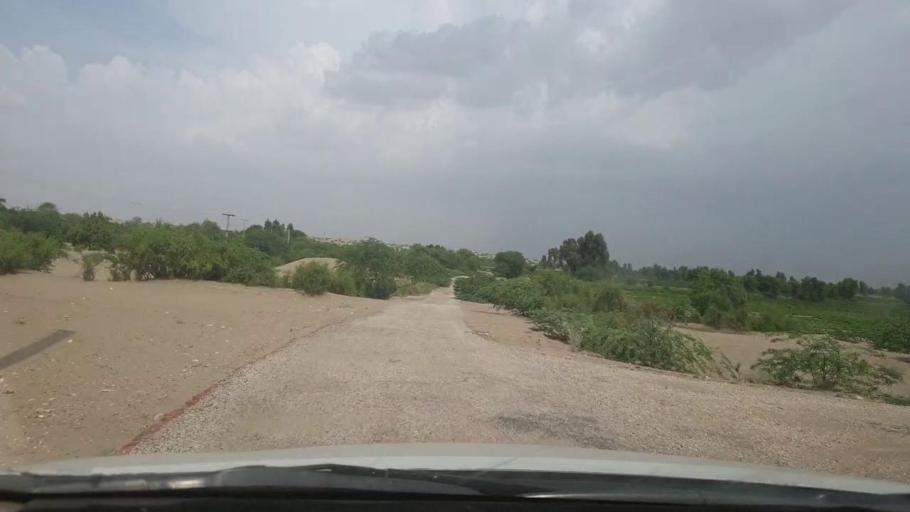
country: PK
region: Sindh
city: Kot Diji
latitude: 27.3379
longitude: 69.0294
